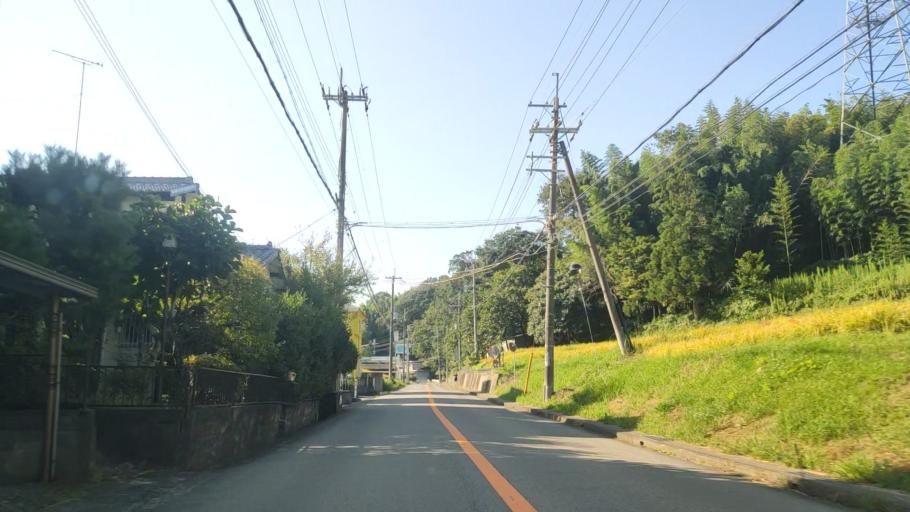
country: JP
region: Hyogo
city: Sandacho
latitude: 34.8156
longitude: 135.2481
